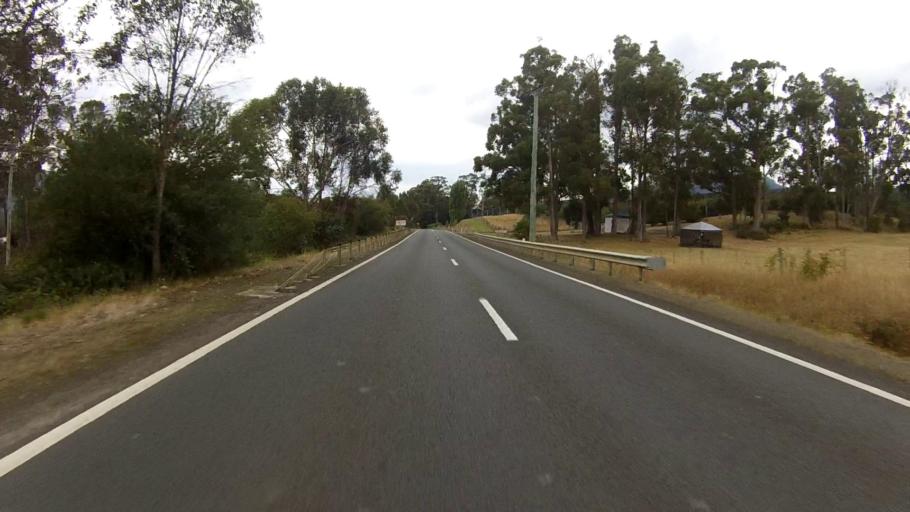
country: AU
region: Tasmania
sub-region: Huon Valley
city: Franklin
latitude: -43.0803
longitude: 147.0319
